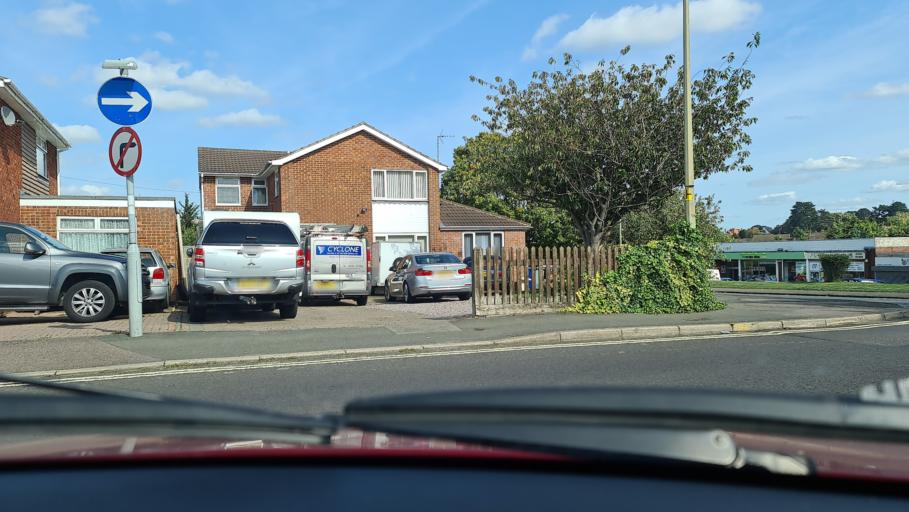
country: GB
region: England
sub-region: Oxfordshire
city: Banbury
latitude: 52.0556
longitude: -1.3507
